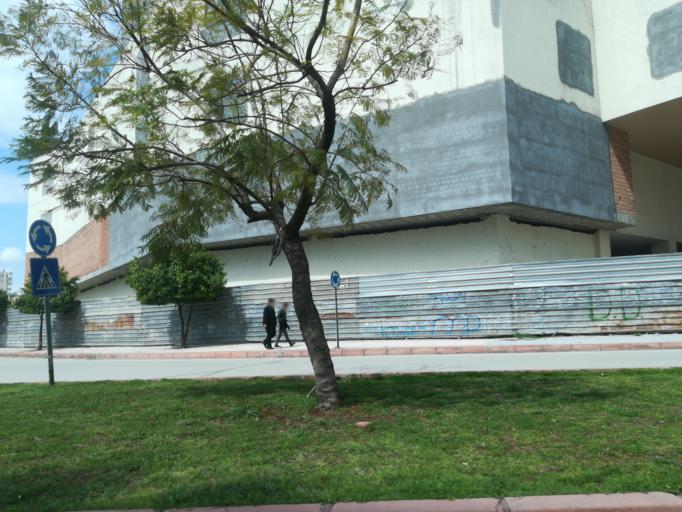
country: TR
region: Adana
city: Adana
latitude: 37.0425
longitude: 35.3018
